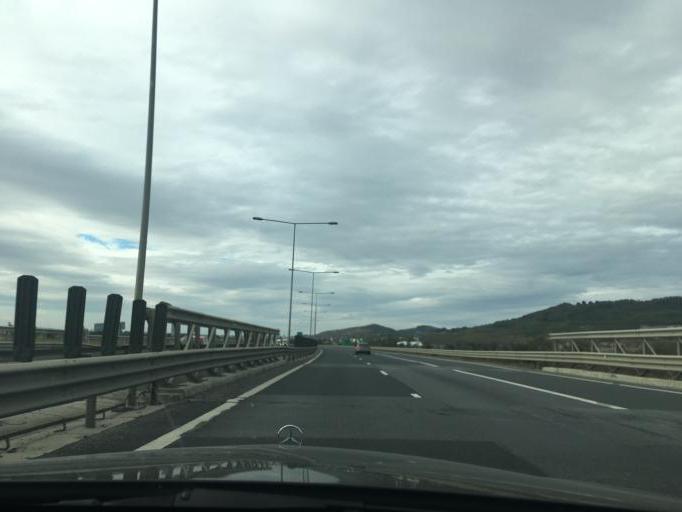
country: RO
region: Sibiu
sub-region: Comuna Selimbar
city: Selimbar
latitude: 45.7925
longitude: 24.1974
